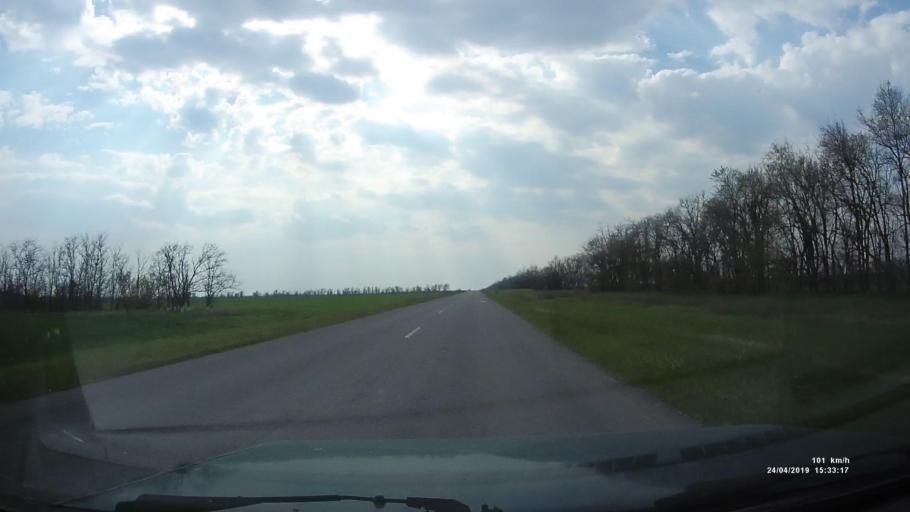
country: RU
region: Rostov
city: Remontnoye
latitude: 46.5995
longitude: 42.9414
